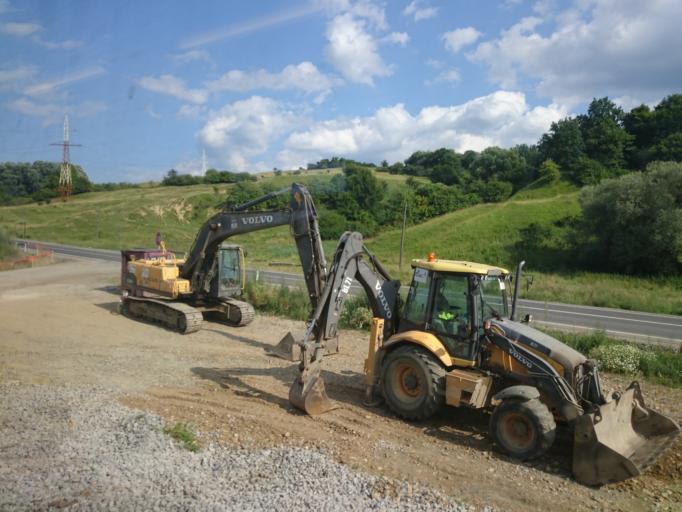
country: RO
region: Sibiu
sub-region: Oras Dumbraveni
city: Dumbraveni
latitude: 46.2169
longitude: 24.5758
